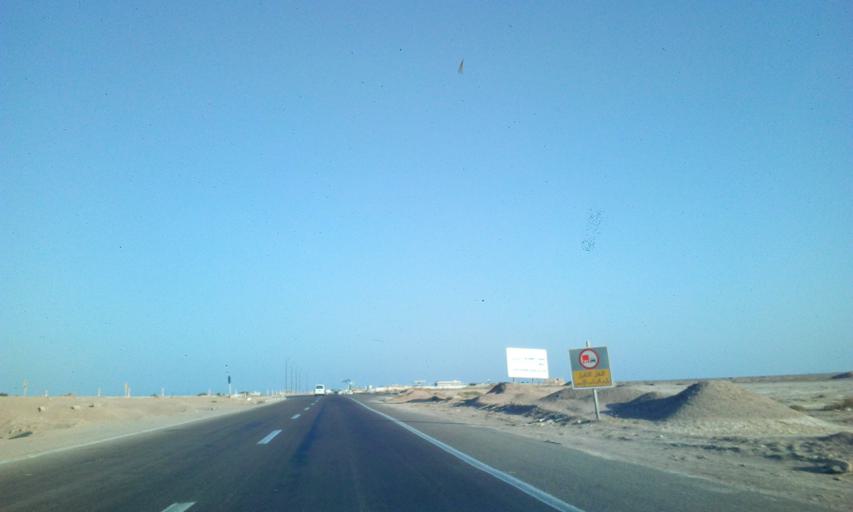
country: EG
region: South Sinai
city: Tor
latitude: 28.3537
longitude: 33.0455
